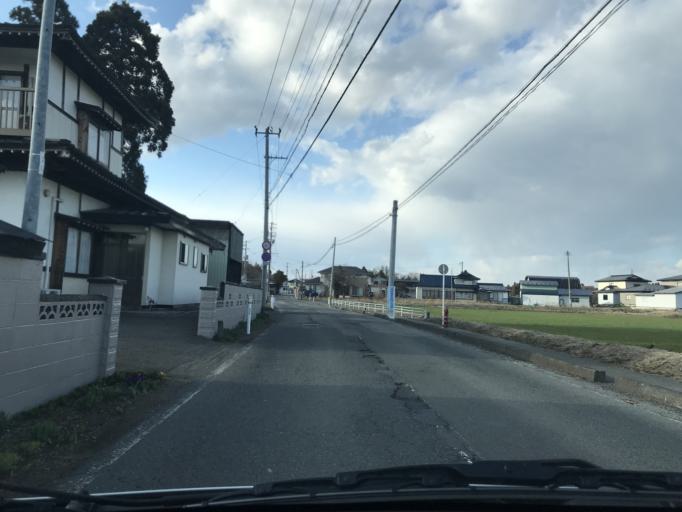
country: JP
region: Iwate
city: Kitakami
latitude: 39.3133
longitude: 141.0690
